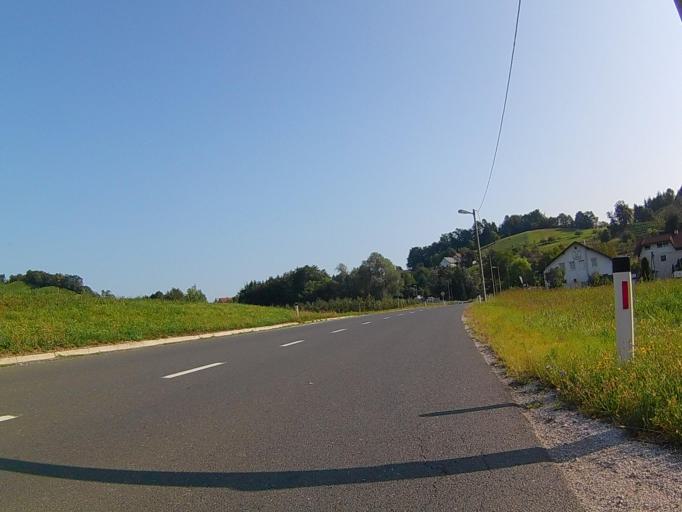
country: SI
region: Maribor
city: Kamnica
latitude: 46.5978
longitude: 15.6197
